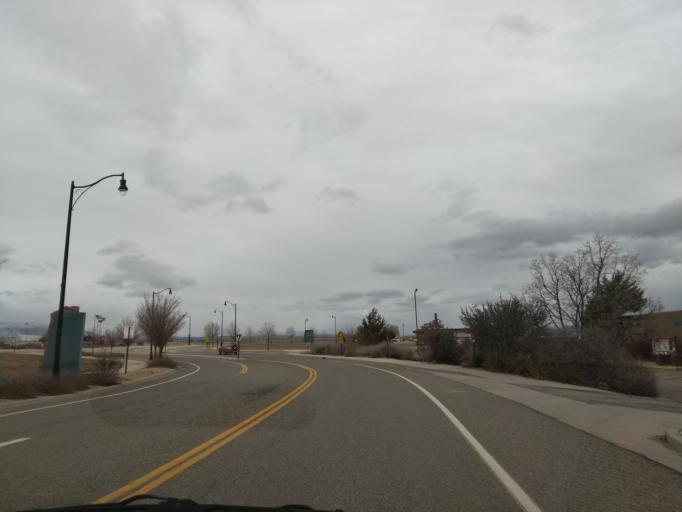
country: US
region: Colorado
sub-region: Mesa County
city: Fruitvale
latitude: 39.1189
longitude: -108.5315
